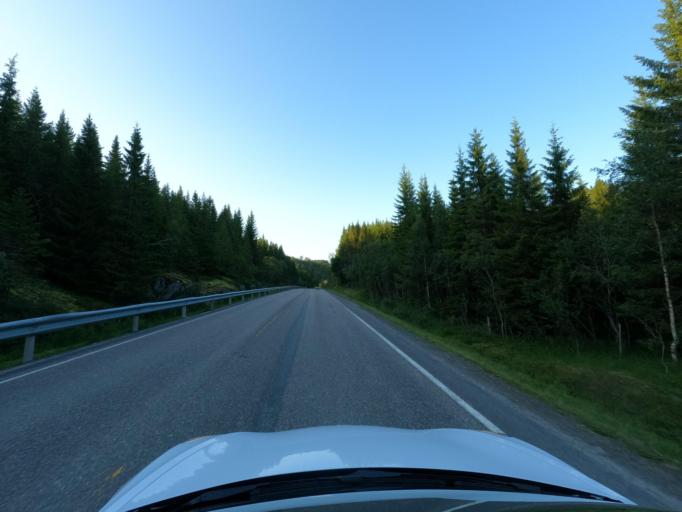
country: NO
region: Troms
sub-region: Harstad
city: Harstad
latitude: 68.7172
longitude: 16.5083
